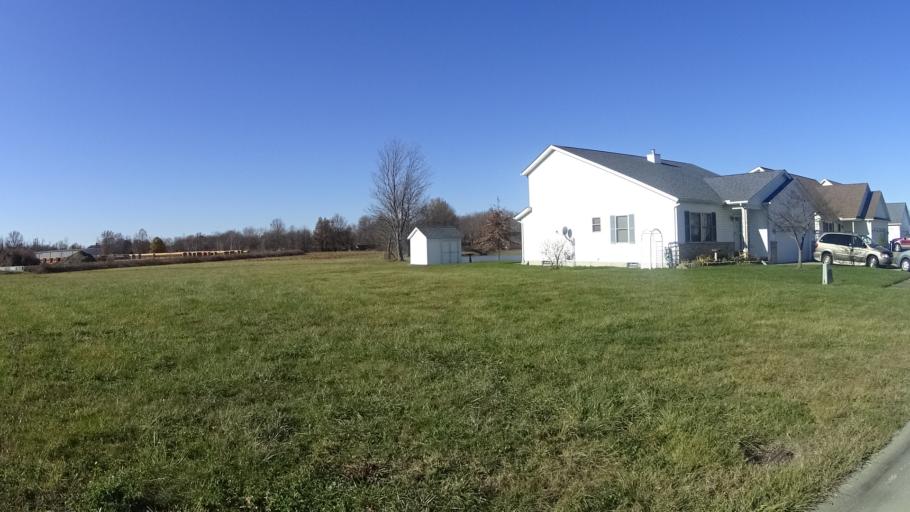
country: US
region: Ohio
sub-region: Lorain County
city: Elyria
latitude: 41.3544
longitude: -82.1431
